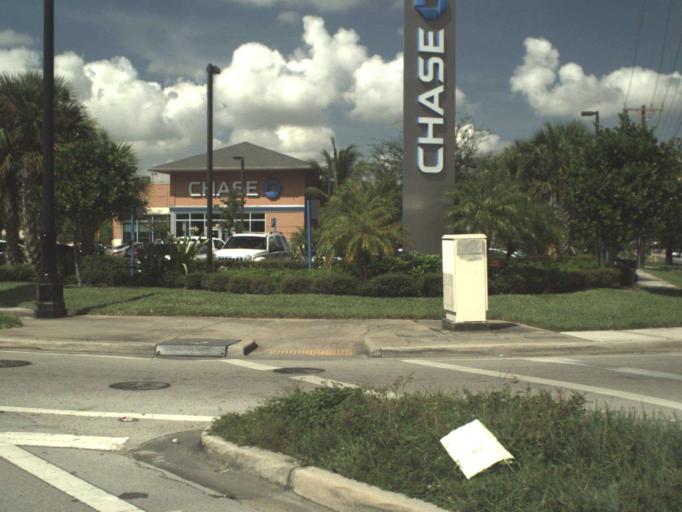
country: US
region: Florida
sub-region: Miami-Dade County
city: Biscayne Park
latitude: 25.8747
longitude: -80.1705
